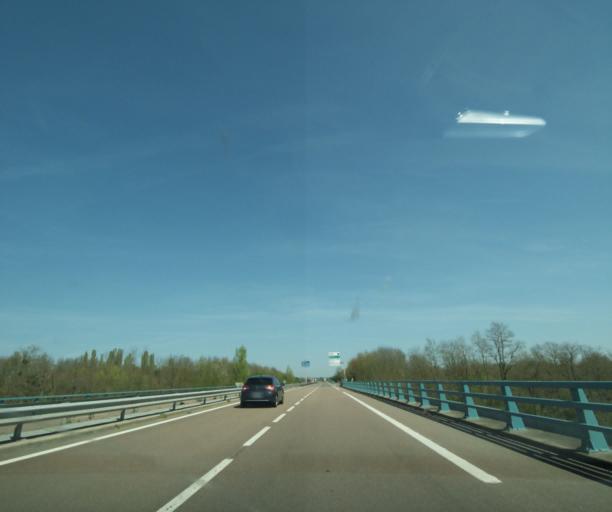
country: FR
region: Bourgogne
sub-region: Departement de la Nievre
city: Saint-Eloi
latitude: 46.9752
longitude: 3.1979
